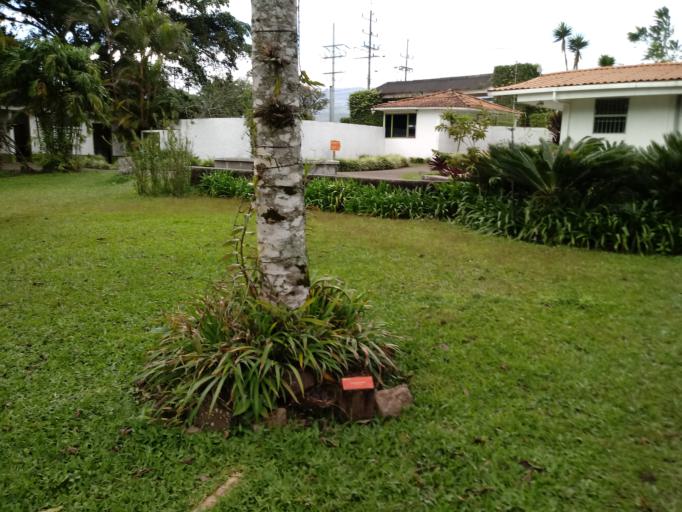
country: CR
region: Cartago
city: Paraiso
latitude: 9.8396
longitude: -83.8883
